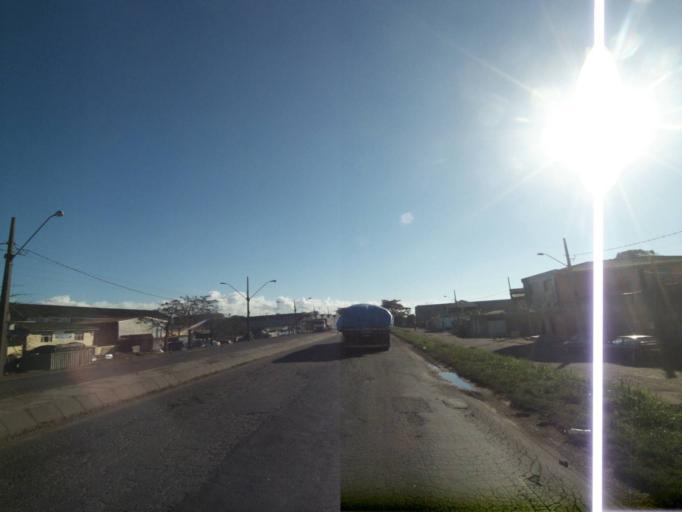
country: BR
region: Parana
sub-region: Paranagua
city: Paranagua
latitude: -25.5185
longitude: -48.5244
